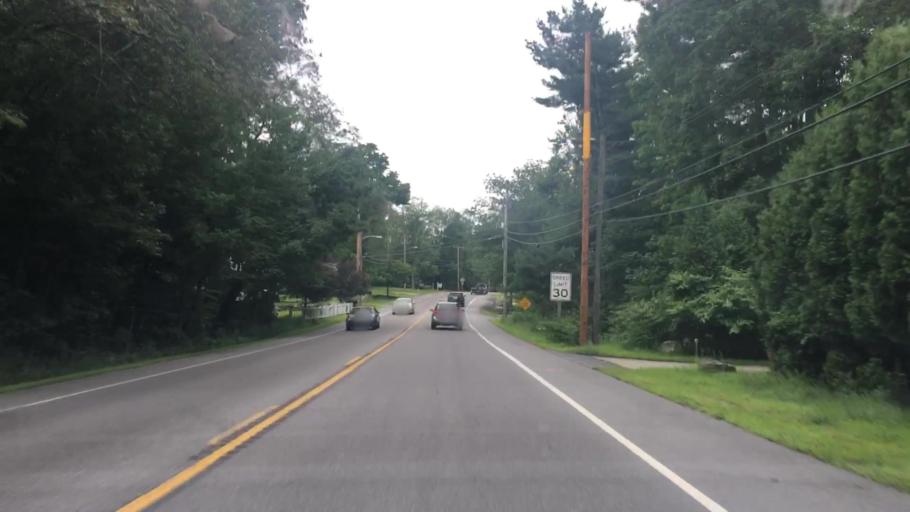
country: US
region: Maine
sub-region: York County
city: Alfred
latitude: 43.4805
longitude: -70.7175
